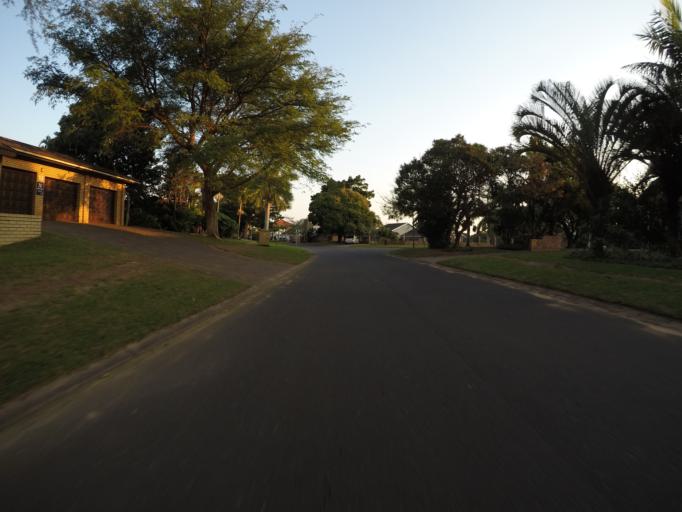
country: ZA
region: KwaZulu-Natal
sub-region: uThungulu District Municipality
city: Richards Bay
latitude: -28.7676
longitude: 32.1172
